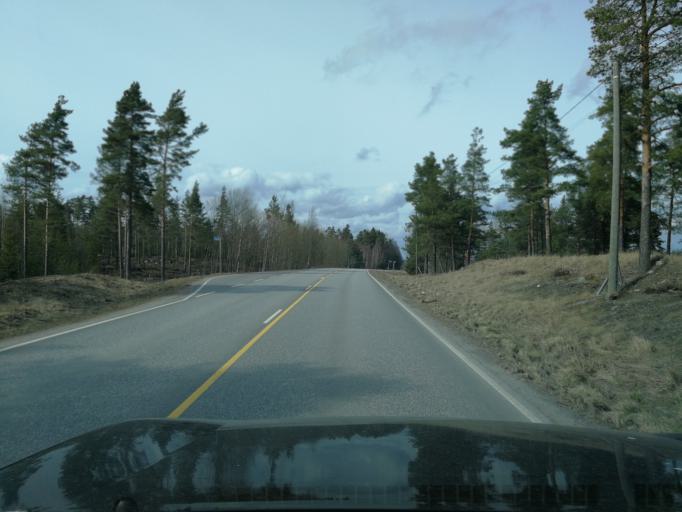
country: FI
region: Uusimaa
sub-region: Helsinki
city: Siuntio
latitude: 60.1020
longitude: 24.2492
